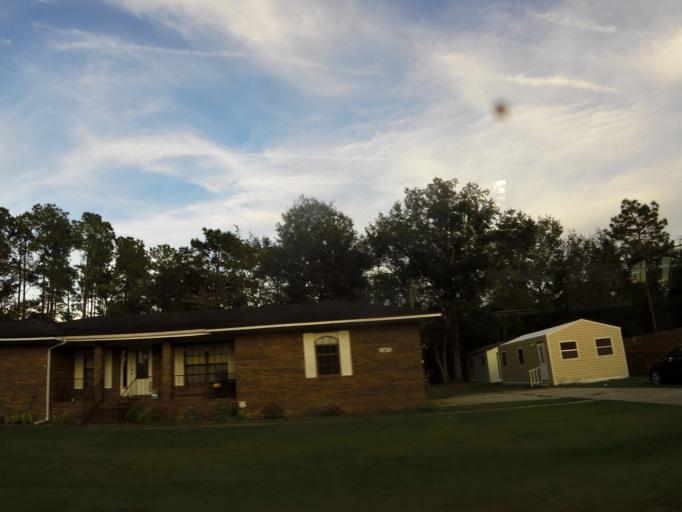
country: US
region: Florida
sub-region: Saint Johns County
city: Fruit Cove
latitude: 30.1616
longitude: -81.5435
